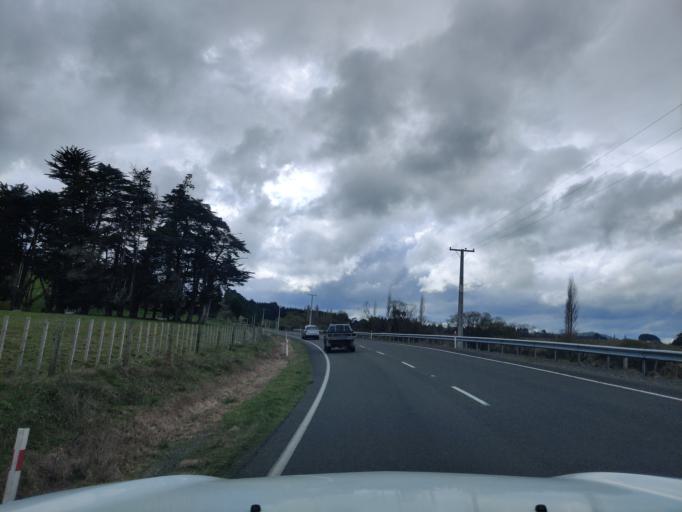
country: NZ
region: Manawatu-Wanganui
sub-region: Ruapehu District
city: Waiouru
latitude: -39.4457
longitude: 175.2903
